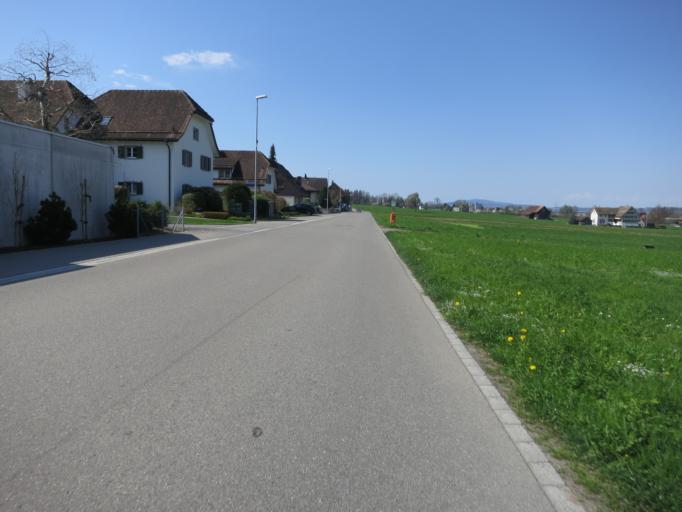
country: CH
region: Schwyz
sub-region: Bezirk March
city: Lachen
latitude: 47.1803
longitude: 8.8683
